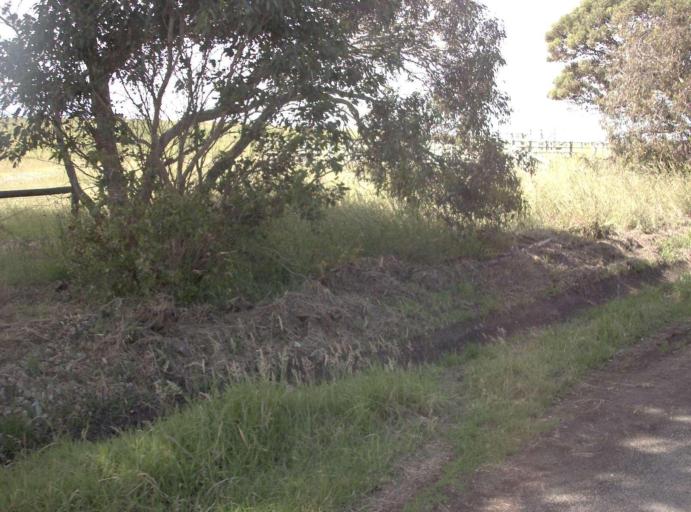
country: AU
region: Victoria
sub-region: Bass Coast
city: Phillip Island
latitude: -38.4972
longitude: 145.1599
